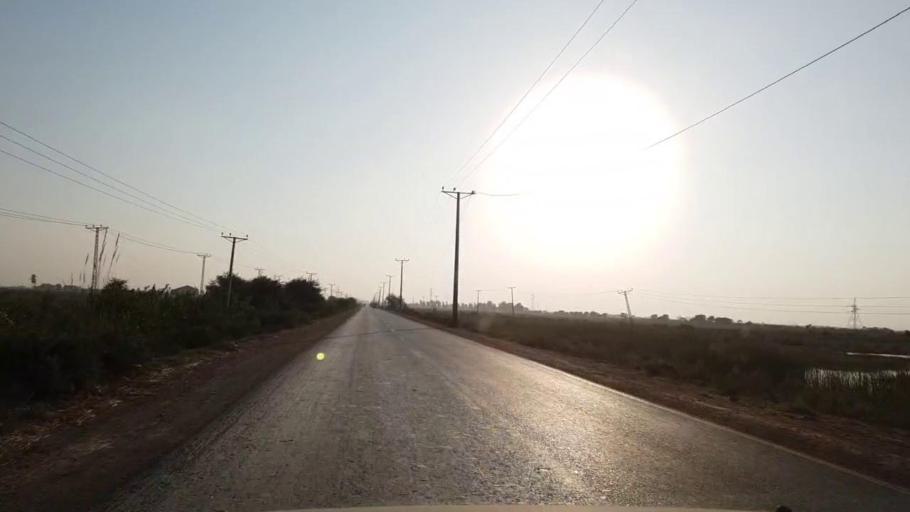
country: PK
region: Sindh
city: Daro Mehar
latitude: 24.6231
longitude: 68.0975
